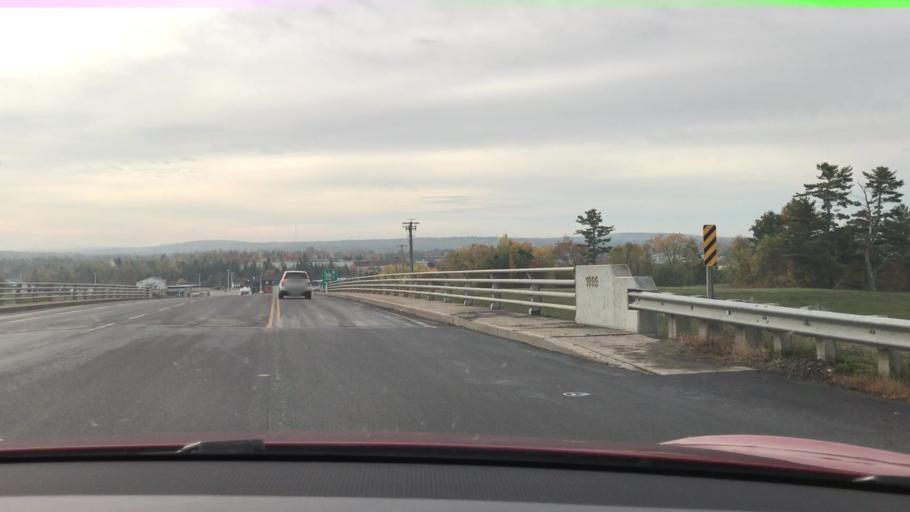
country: US
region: Maine
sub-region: Washington County
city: Calais
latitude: 45.2113
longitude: -67.2729
